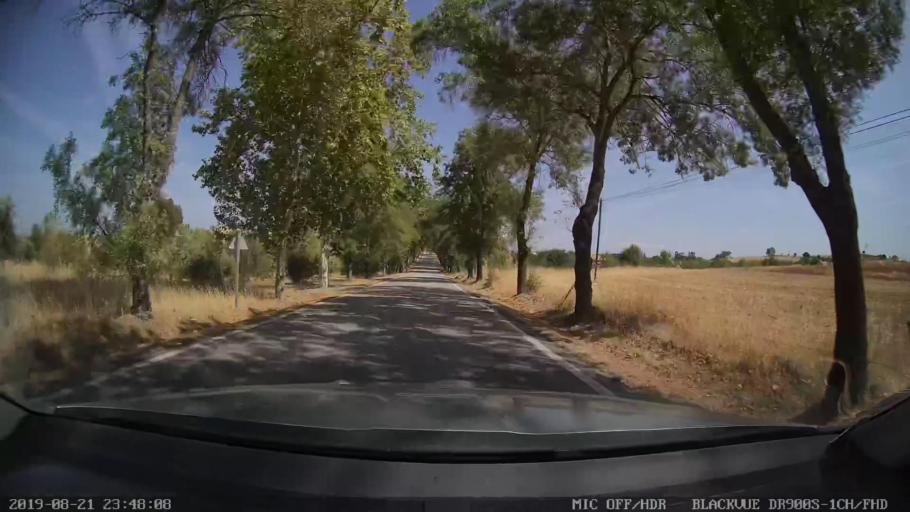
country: PT
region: Castelo Branco
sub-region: Idanha-A-Nova
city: Idanha-a-Nova
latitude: 39.8604
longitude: -7.2587
